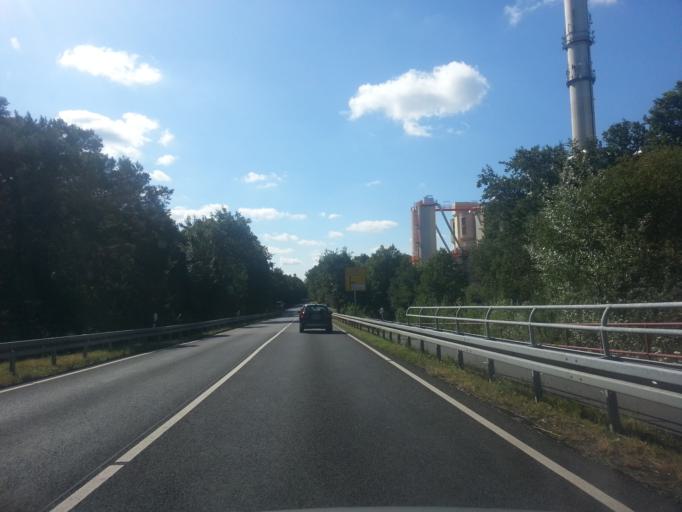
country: DE
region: Hesse
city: Heusenstamm
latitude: 50.0667
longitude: 8.7688
